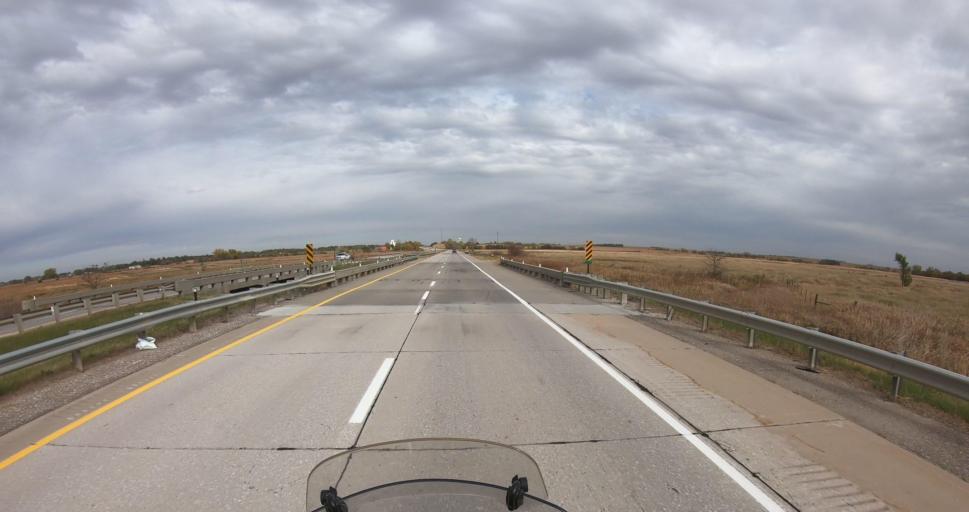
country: US
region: Nebraska
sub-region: Lancaster County
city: Waverly
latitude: 41.0357
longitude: -96.6399
